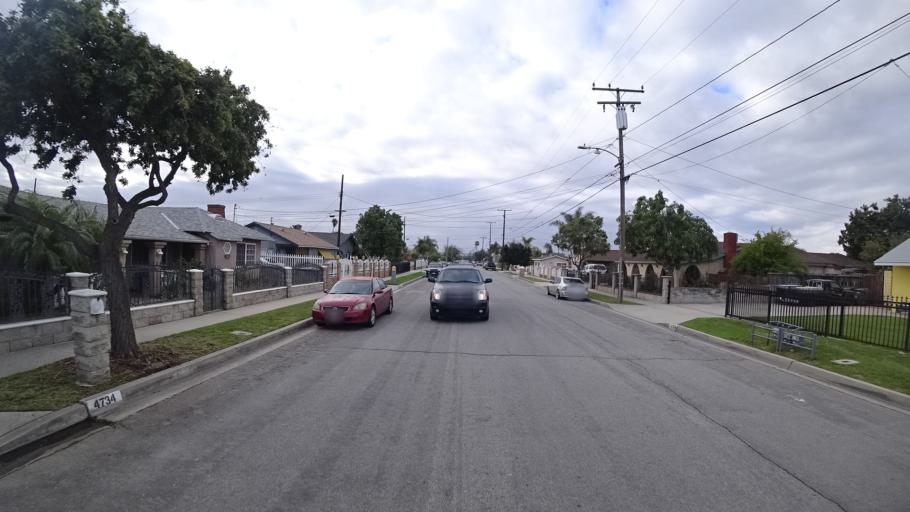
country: US
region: California
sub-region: Los Angeles County
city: Baldwin Park
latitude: 34.0985
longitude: -117.9715
